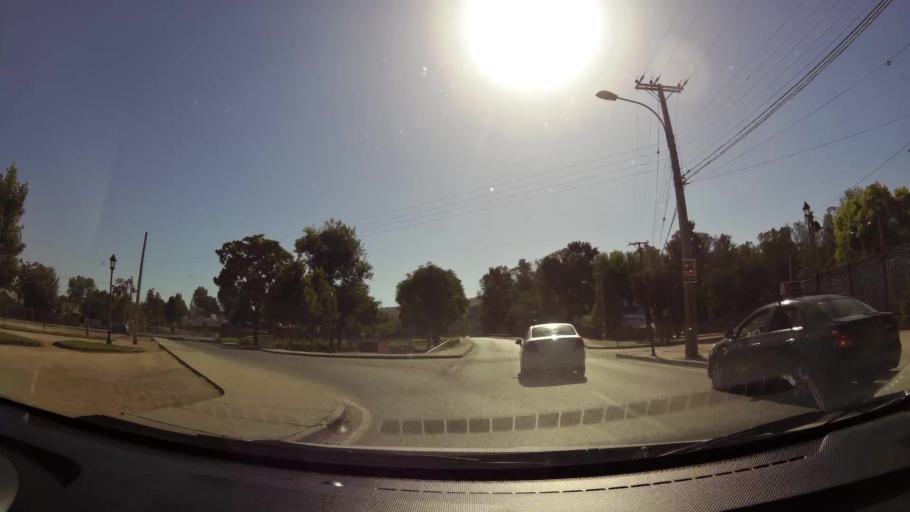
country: CL
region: Maule
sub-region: Provincia de Talca
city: Talca
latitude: -35.4206
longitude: -71.6786
